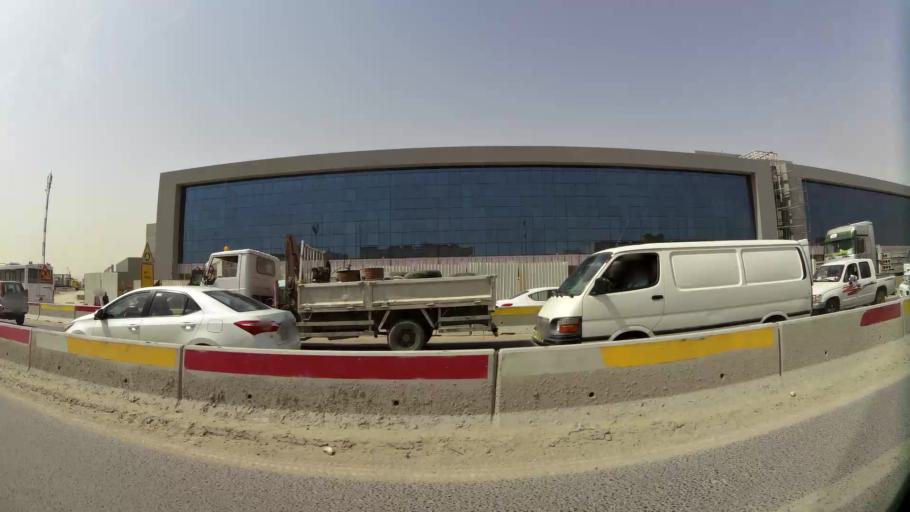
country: QA
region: Baladiyat ar Rayyan
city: Ar Rayyan
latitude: 25.1875
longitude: 51.4372
